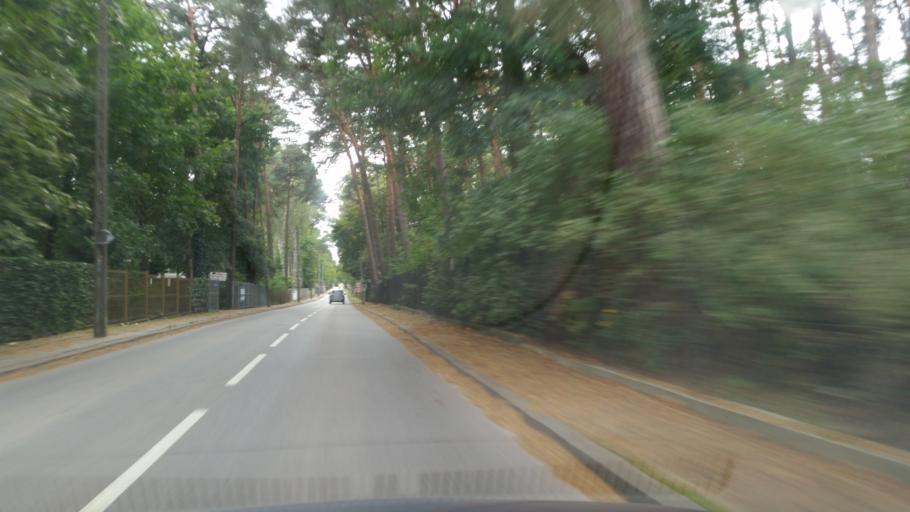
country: PL
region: Masovian Voivodeship
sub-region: Powiat piaseczynski
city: Konstancin-Jeziorna
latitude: 52.0758
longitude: 21.0985
